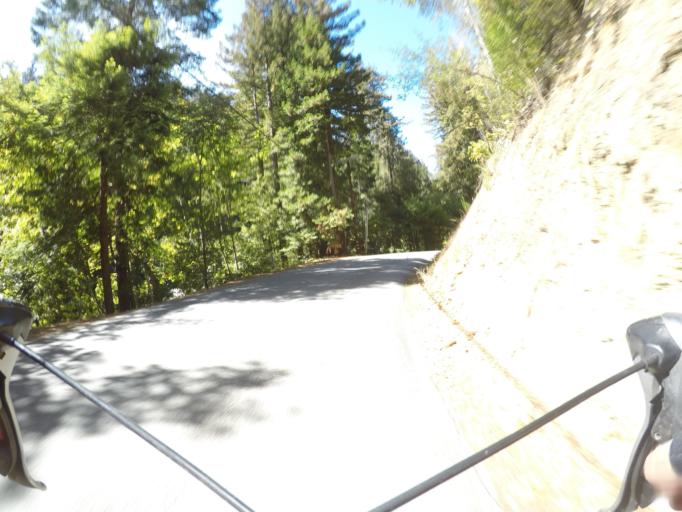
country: US
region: California
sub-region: San Mateo County
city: Portola Valley
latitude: 37.2974
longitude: -122.2612
